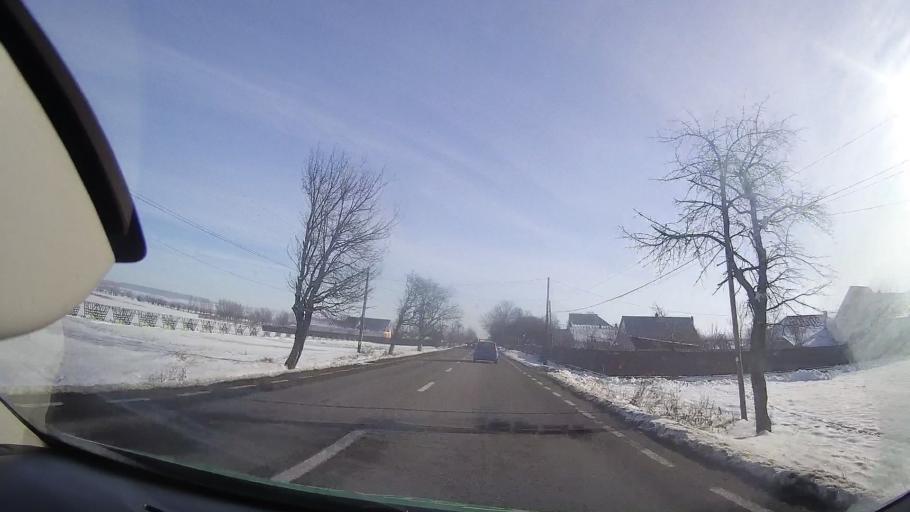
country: RO
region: Neamt
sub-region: Comuna Negresti
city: Negresti
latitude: 47.0594
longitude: 26.3870
